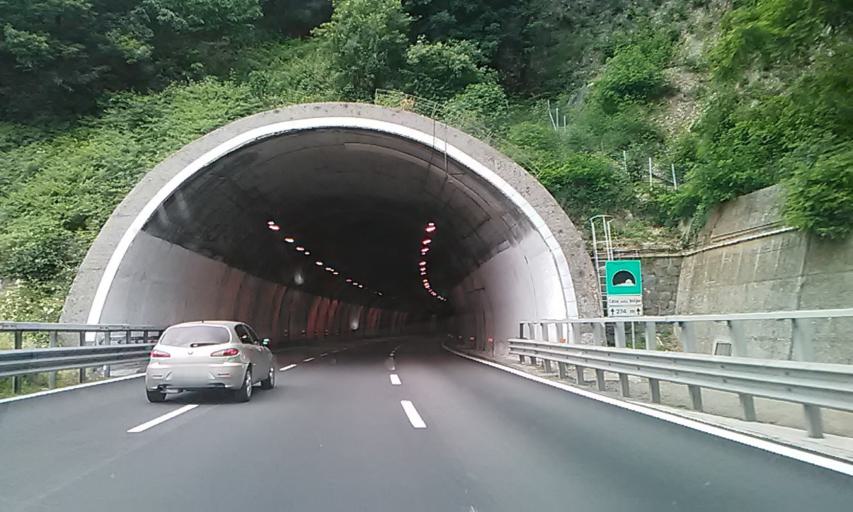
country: IT
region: Liguria
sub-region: Provincia di Genova
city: Mele
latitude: 44.4482
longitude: 8.7374
